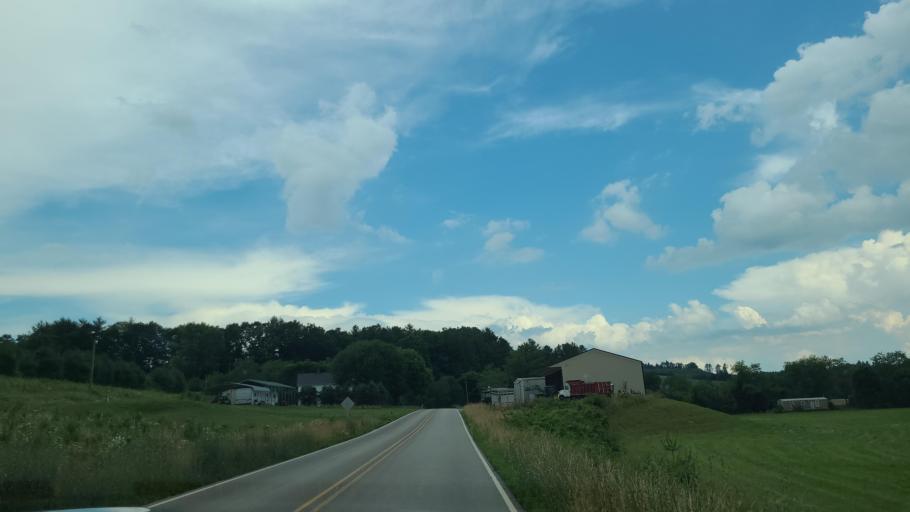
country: US
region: North Carolina
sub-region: Alleghany County
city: Sparta
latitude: 36.4180
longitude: -81.2690
